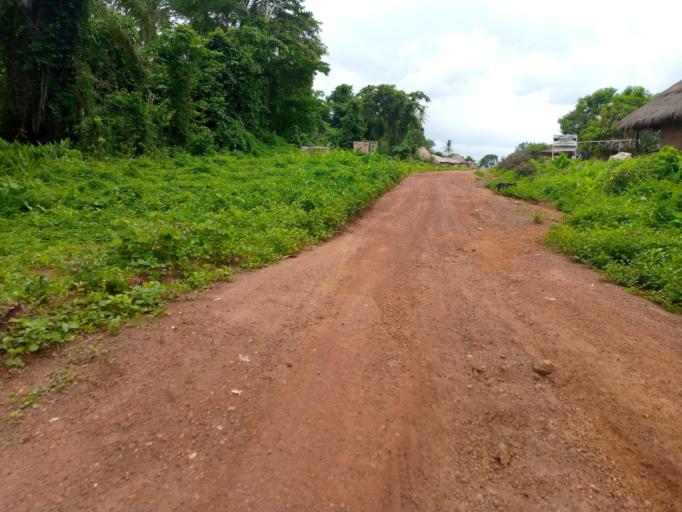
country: SL
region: Southern Province
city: Moyamba
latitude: 8.0883
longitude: -12.4485
